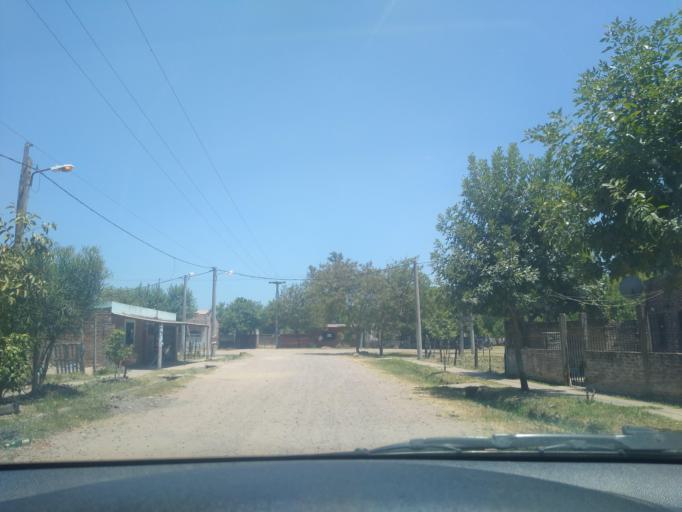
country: AR
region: Chaco
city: Fontana
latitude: -27.4092
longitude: -59.0541
